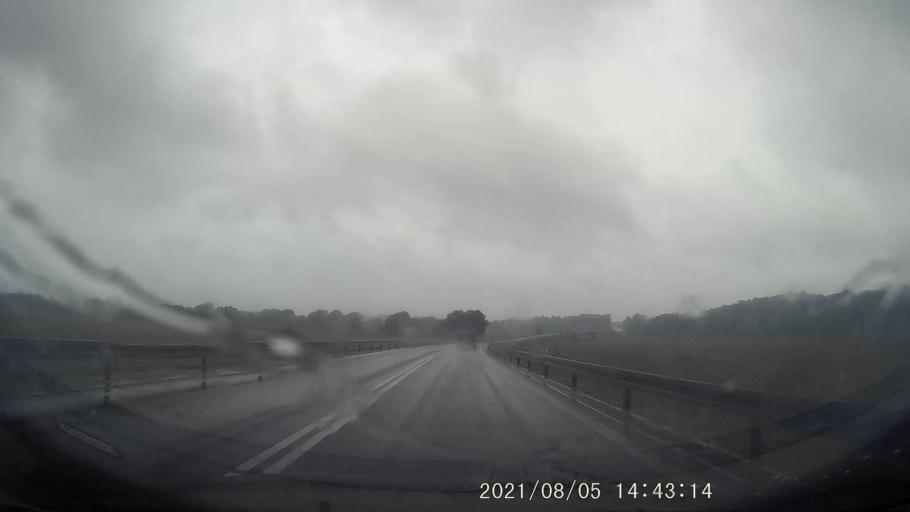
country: PL
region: Opole Voivodeship
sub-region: Powiat nyski
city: Nysa
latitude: 50.4811
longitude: 17.3925
